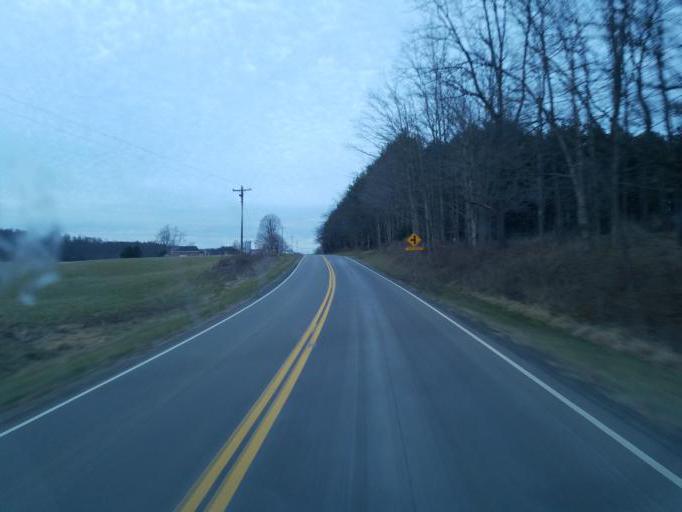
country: US
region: Ohio
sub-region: Muskingum County
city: Dresden
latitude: 40.1872
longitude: -82.0357
